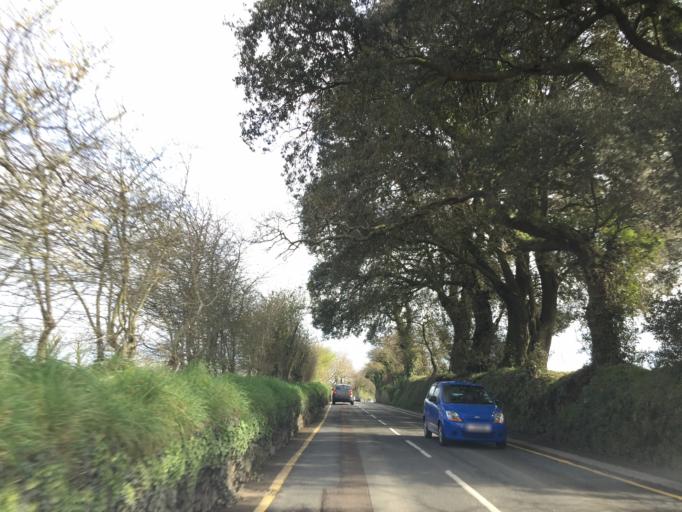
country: JE
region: St Helier
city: Saint Helier
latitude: 49.2009
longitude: -2.0766
